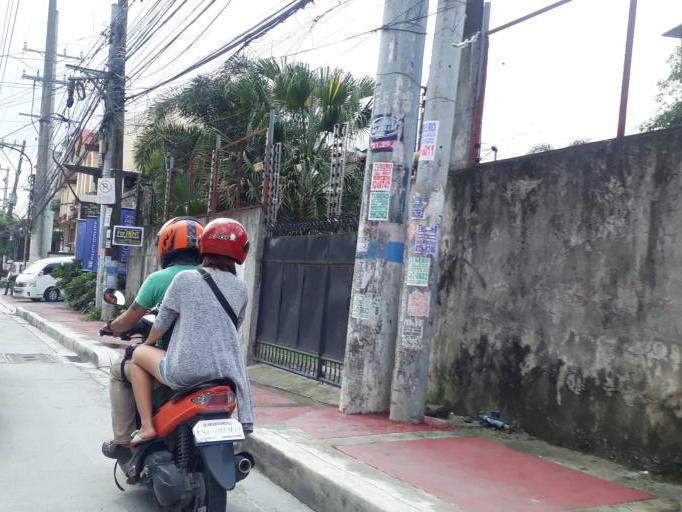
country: PH
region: Metro Manila
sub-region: San Juan
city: San Juan
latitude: 14.6159
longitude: 121.0451
